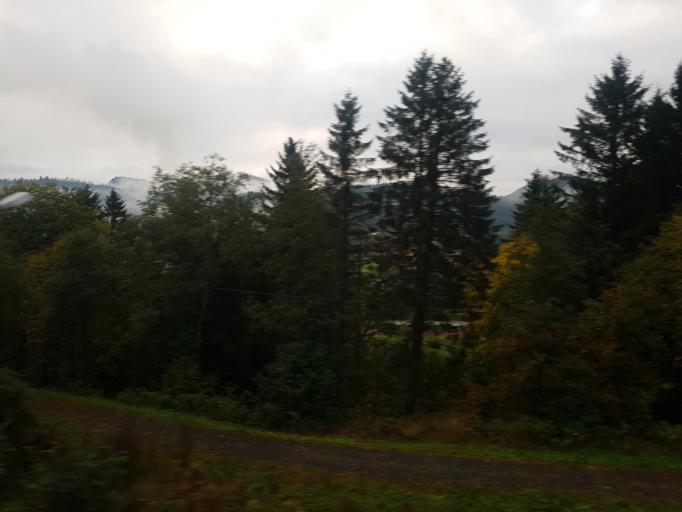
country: NO
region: Sor-Trondelag
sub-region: Midtre Gauldal
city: Storen
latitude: 63.0380
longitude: 10.2798
